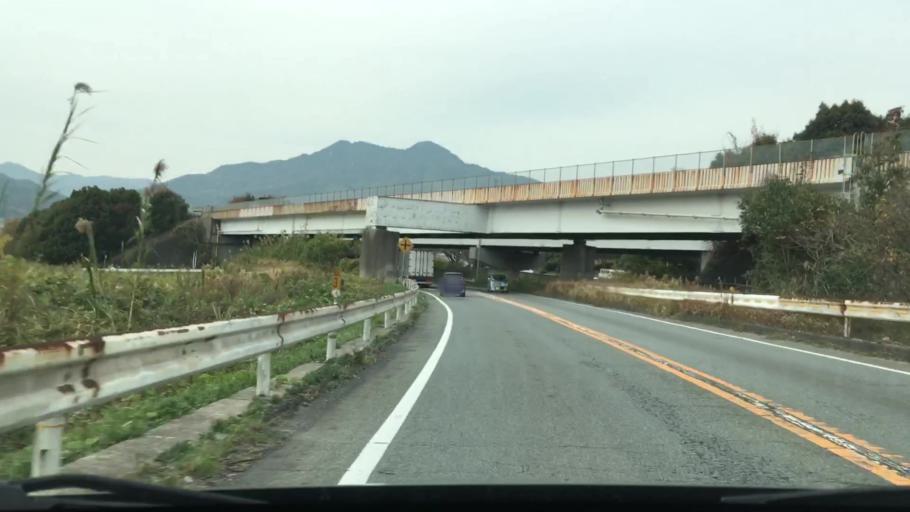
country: JP
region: Yamaguchi
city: Hofu
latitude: 34.0574
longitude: 131.6153
